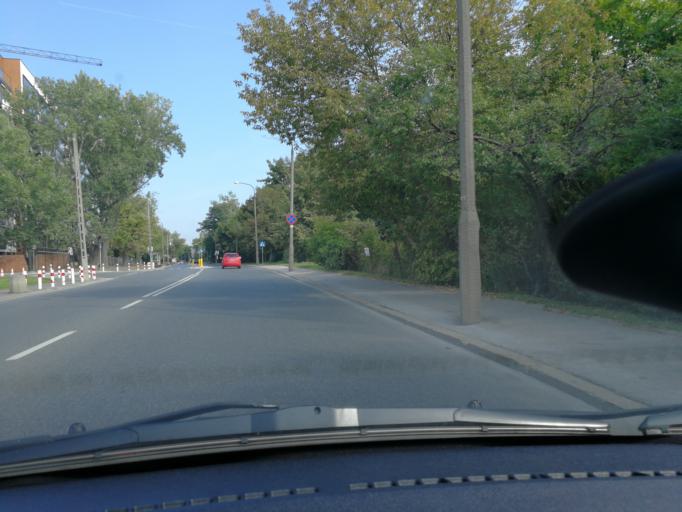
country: PL
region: Masovian Voivodeship
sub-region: Warszawa
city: Bemowo
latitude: 52.2291
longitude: 20.9424
